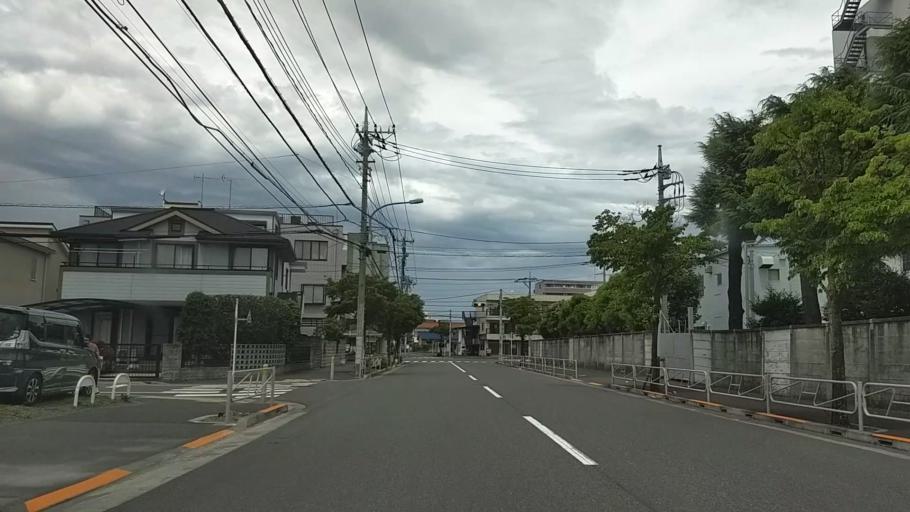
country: JP
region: Tokyo
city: Hachioji
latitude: 35.6475
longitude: 139.3549
